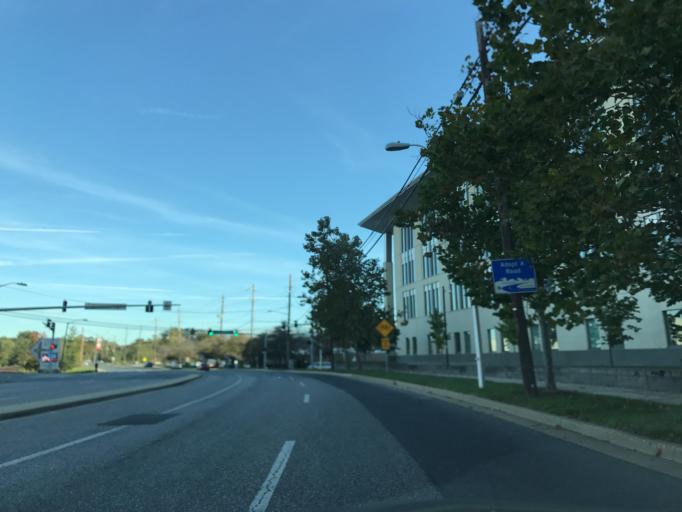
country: US
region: Maryland
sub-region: Prince George's County
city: College Park
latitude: 38.9778
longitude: -76.9262
